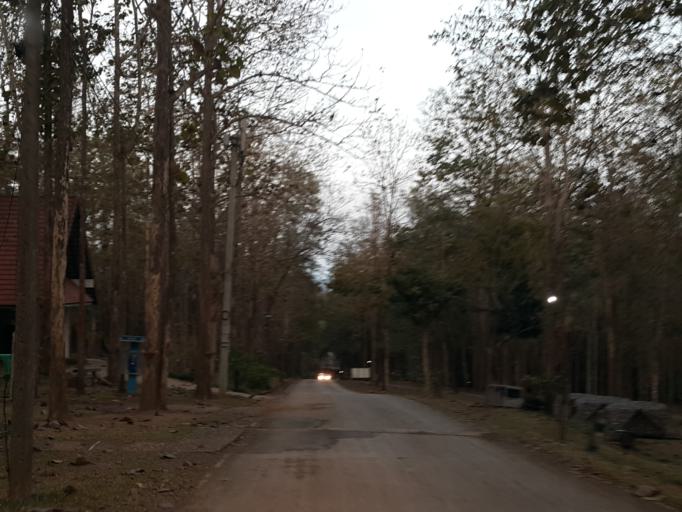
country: TH
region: Lampang
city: Mueang Pan
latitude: 18.8330
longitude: 99.4674
